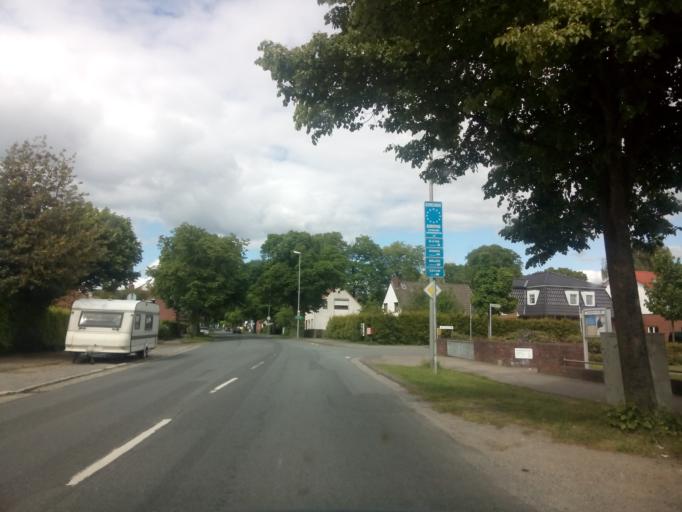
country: DE
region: Lower Saxony
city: Ritterhude
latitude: 53.1790
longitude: 8.7316
